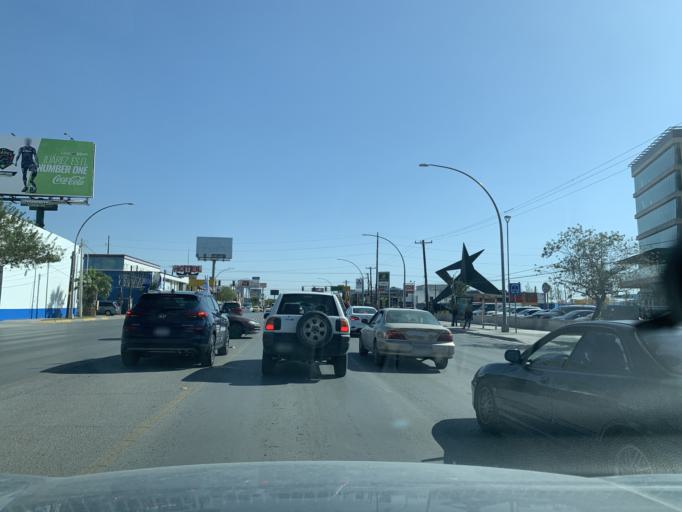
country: MX
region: Chihuahua
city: Ciudad Juarez
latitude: 31.7384
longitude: -106.4344
